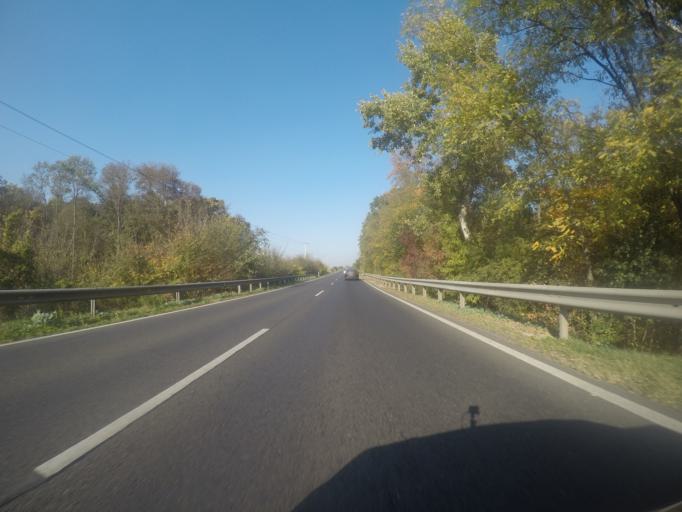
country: HU
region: Fejer
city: Baracs
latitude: 46.8533
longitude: 18.9125
